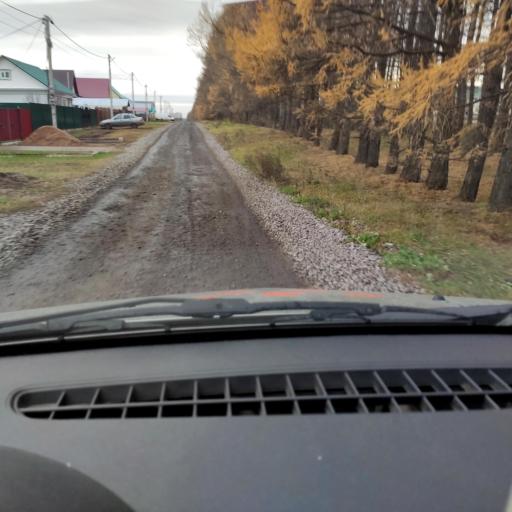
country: RU
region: Bashkortostan
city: Ufa
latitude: 54.8531
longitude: 56.0110
